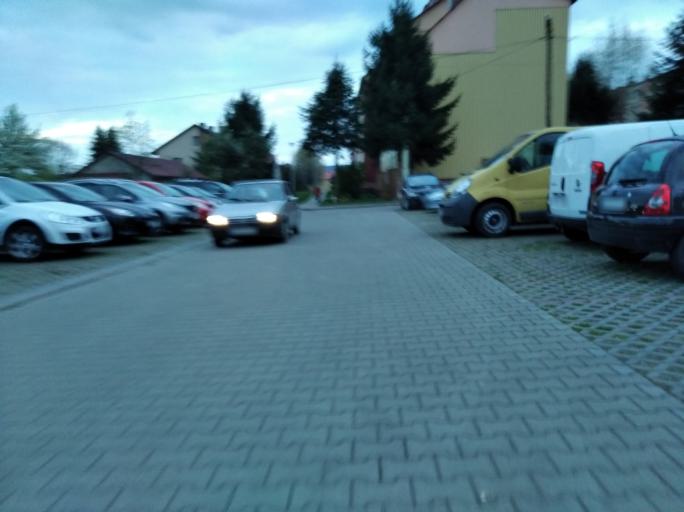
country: PL
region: Subcarpathian Voivodeship
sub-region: Powiat strzyzowski
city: Strzyzow
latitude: 49.8725
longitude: 21.7936
